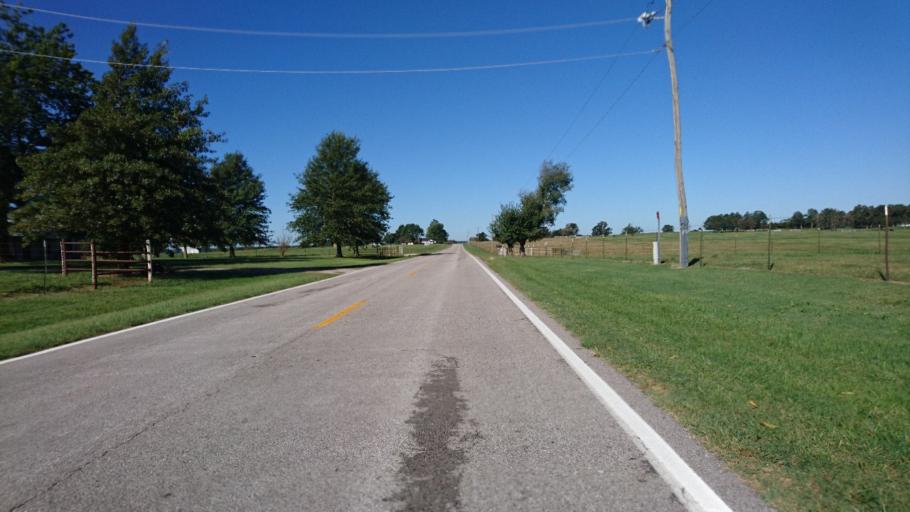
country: US
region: Missouri
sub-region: Greene County
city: Ash Grove
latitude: 37.1940
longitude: -93.6606
